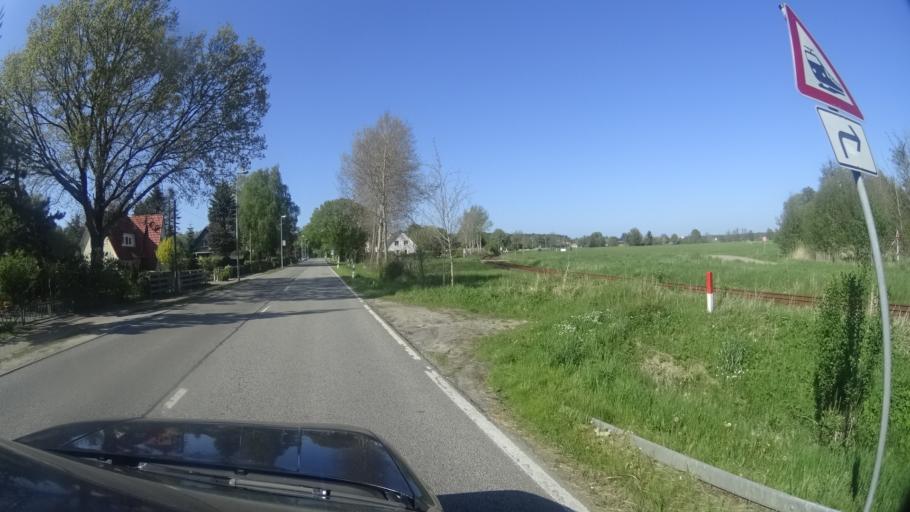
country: DE
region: Mecklenburg-Vorpommern
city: Seeheilbad Graal-Muritz
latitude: 54.2392
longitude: 12.2249
